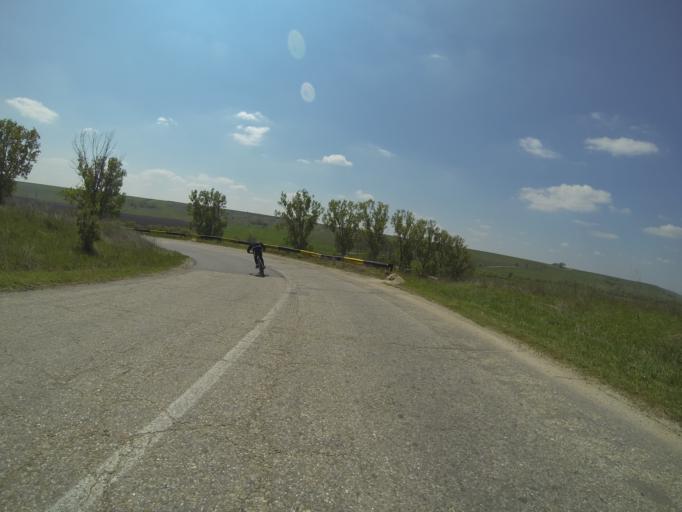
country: RO
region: Dolj
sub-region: Comuna Salcuta
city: Salcuta
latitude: 44.2595
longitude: 23.4556
